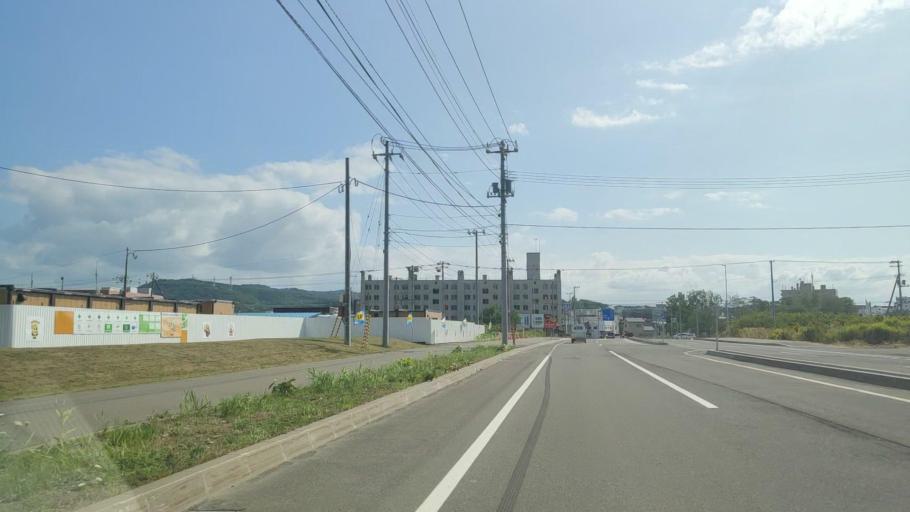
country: JP
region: Hokkaido
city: Rumoi
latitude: 43.9440
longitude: 141.6477
